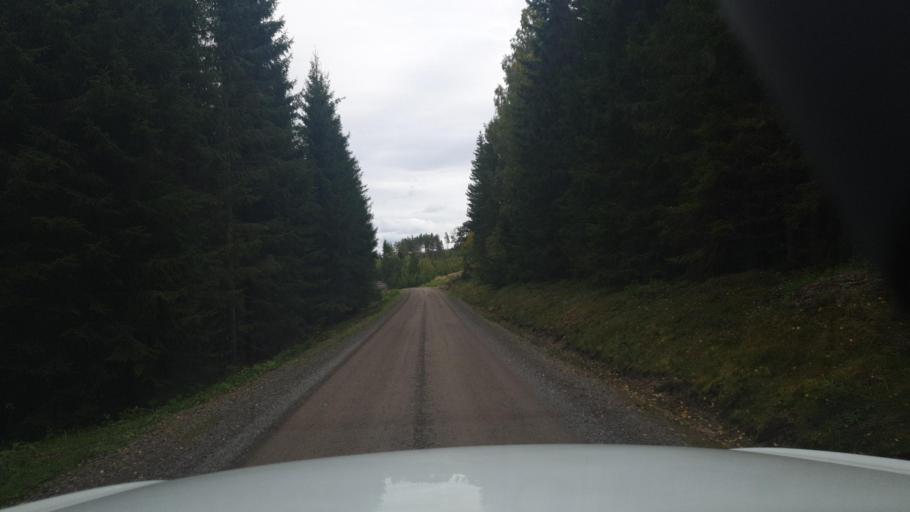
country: SE
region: Vaermland
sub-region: Torsby Kommun
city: Torsby
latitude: 59.9806
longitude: 12.8399
